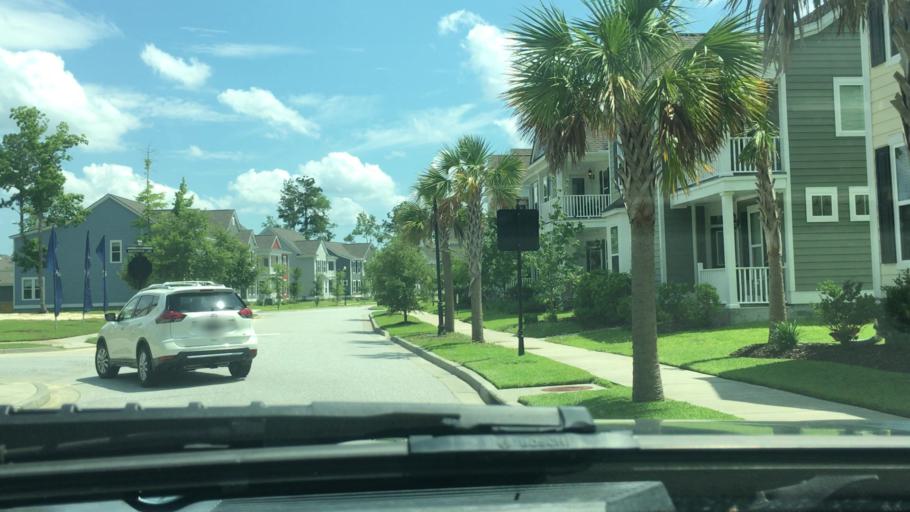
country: US
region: South Carolina
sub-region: Charleston County
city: Shell Point
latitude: 32.8088
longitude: -80.0740
